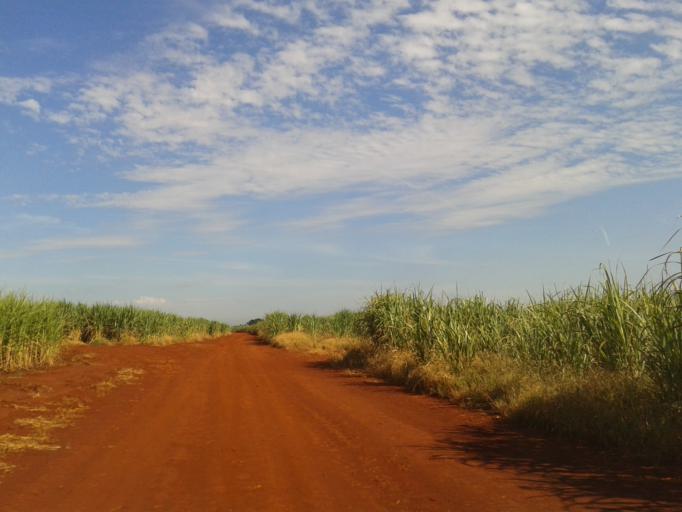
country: BR
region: Minas Gerais
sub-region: Centralina
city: Centralina
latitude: -18.6392
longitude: -49.2450
